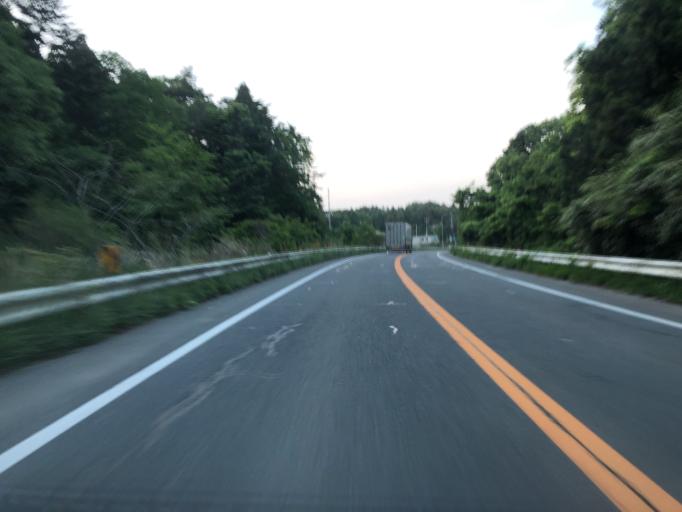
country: JP
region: Fukushima
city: Namie
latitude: 37.5327
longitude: 141.0020
